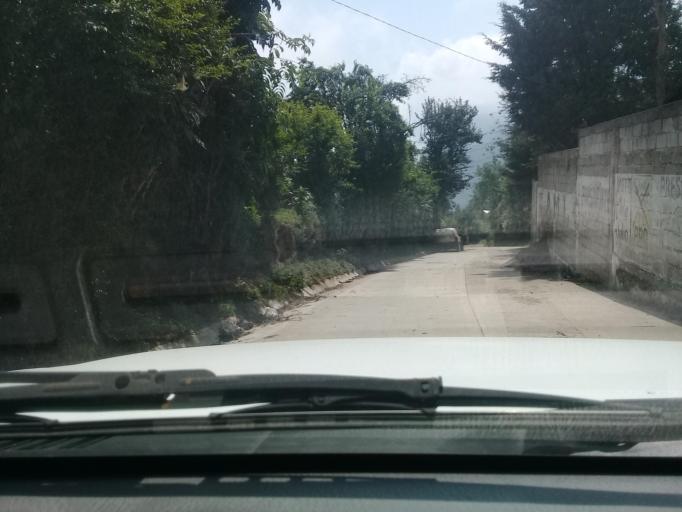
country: MX
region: Veracruz
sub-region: Mariano Escobedo
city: San Isidro el Berro
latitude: 18.9461
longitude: -97.2093
